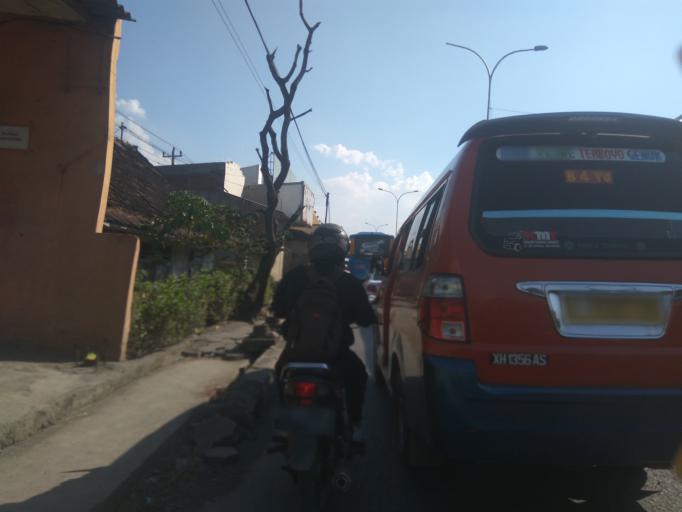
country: ID
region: Central Java
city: Semarang
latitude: -6.9522
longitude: 110.4787
